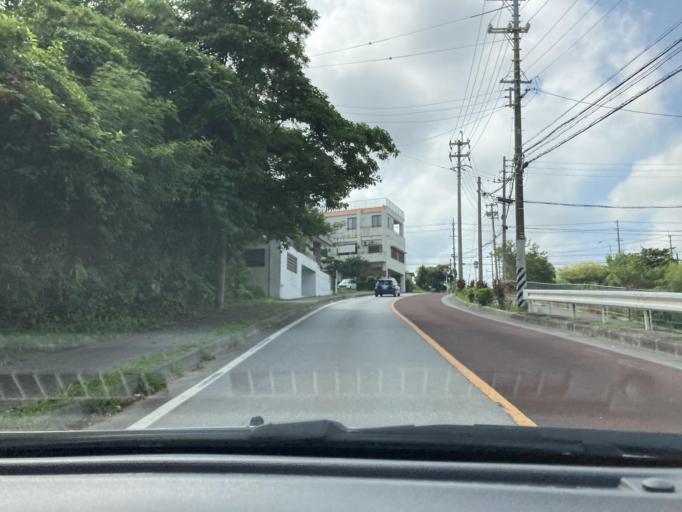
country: JP
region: Okinawa
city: Okinawa
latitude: 26.3188
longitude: 127.8048
